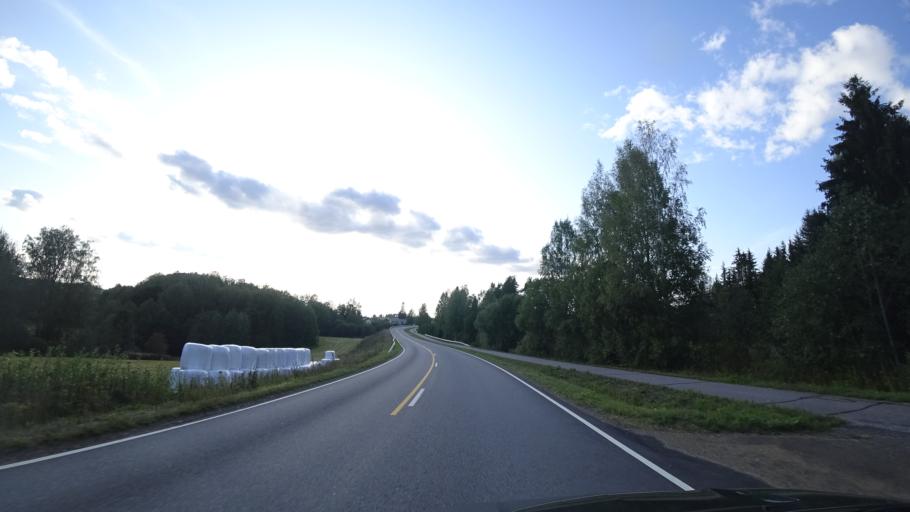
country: FI
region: Haeme
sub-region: Haemeenlinna
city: Lammi
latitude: 61.0809
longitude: 25.0622
